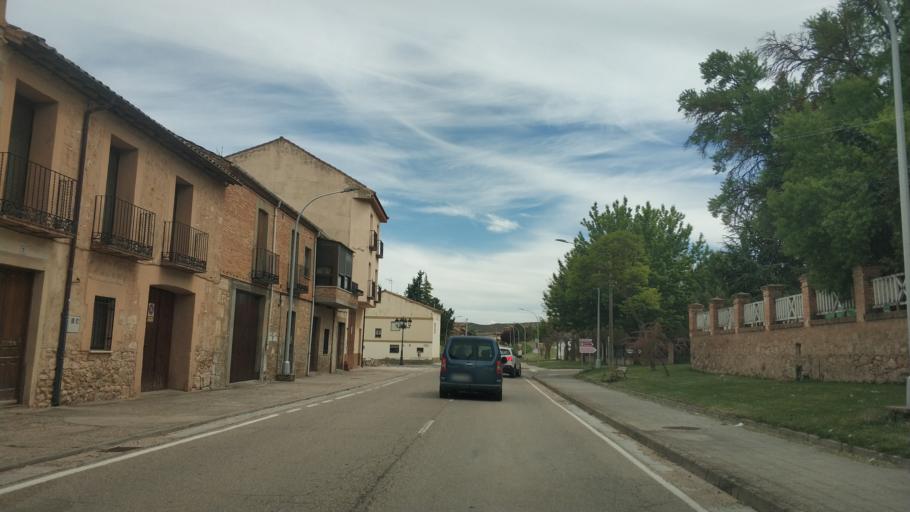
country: ES
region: Castille and Leon
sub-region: Provincia de Soria
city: Berlanga de Duero
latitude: 41.4645
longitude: -2.8626
